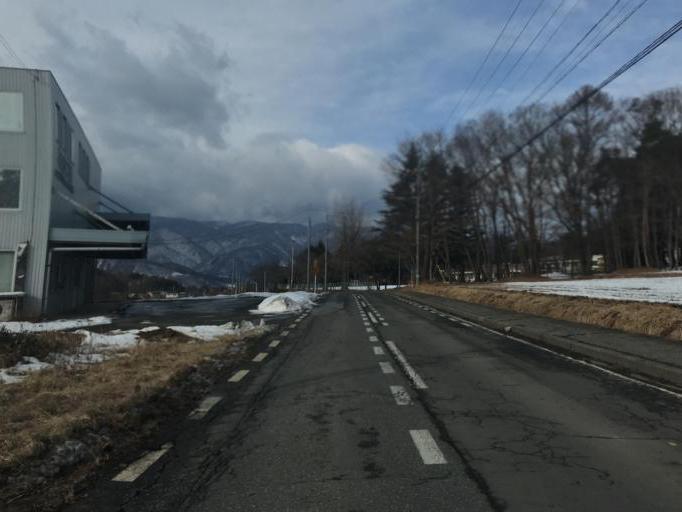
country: JP
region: Nagano
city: Chino
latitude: 35.8891
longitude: 138.2904
